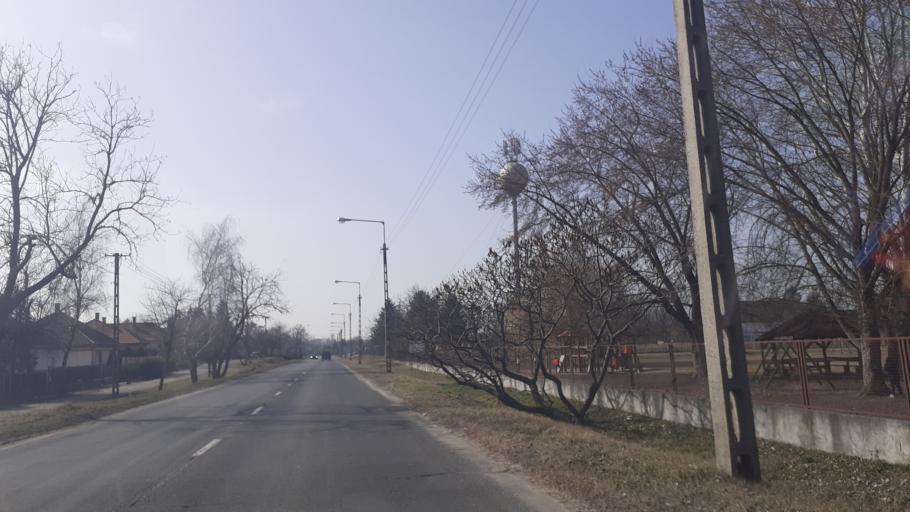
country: HU
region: Pest
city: Orkeny
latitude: 47.1329
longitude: 19.4354
